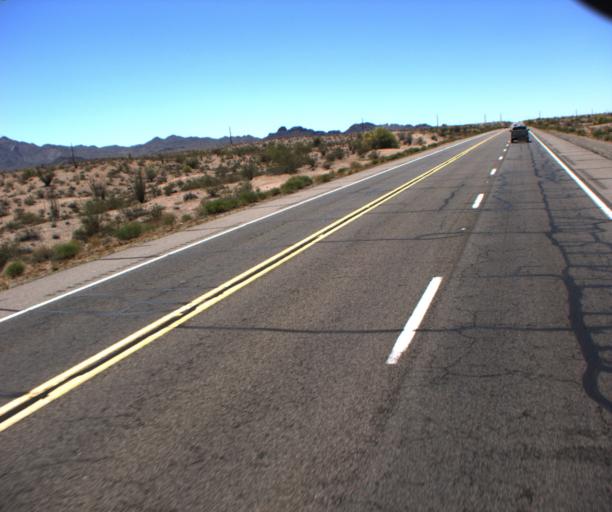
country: US
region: Arizona
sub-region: Mohave County
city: Desert Hills
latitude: 34.6801
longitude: -114.3062
